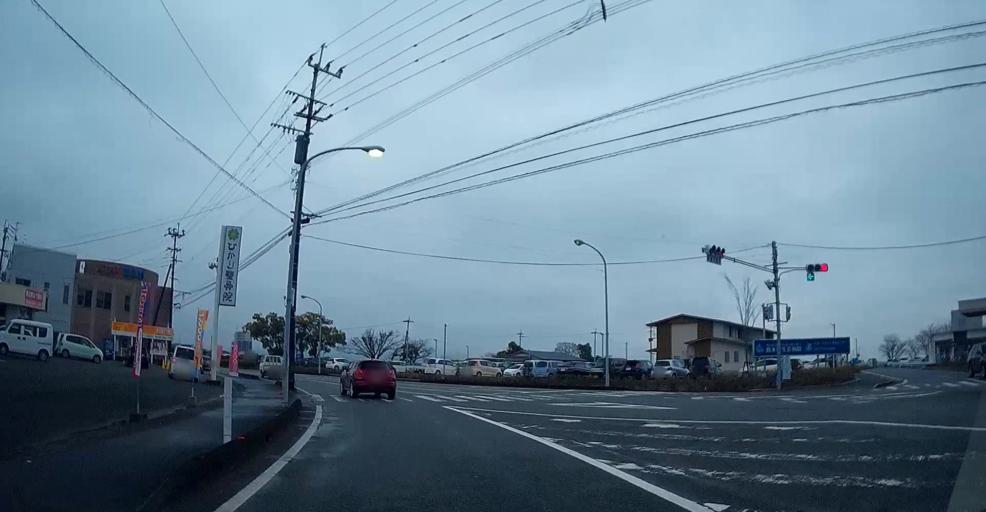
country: JP
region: Kumamoto
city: Kumamoto
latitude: 32.7480
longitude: 130.7382
